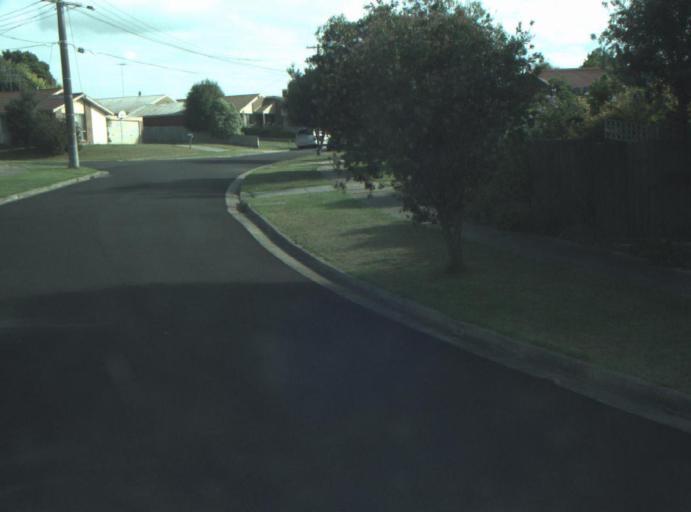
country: AU
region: Victoria
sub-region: Greater Geelong
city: Wandana Heights
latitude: -38.2122
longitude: 144.3201
